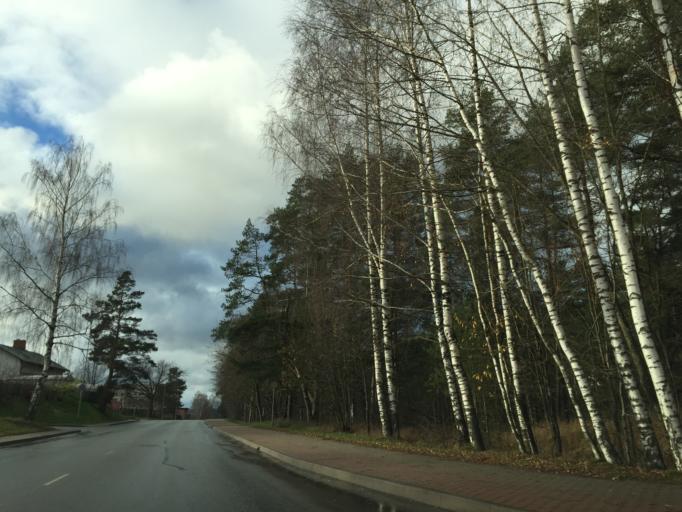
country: LV
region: Valmieras Rajons
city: Valmiera
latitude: 57.5296
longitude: 25.4454
